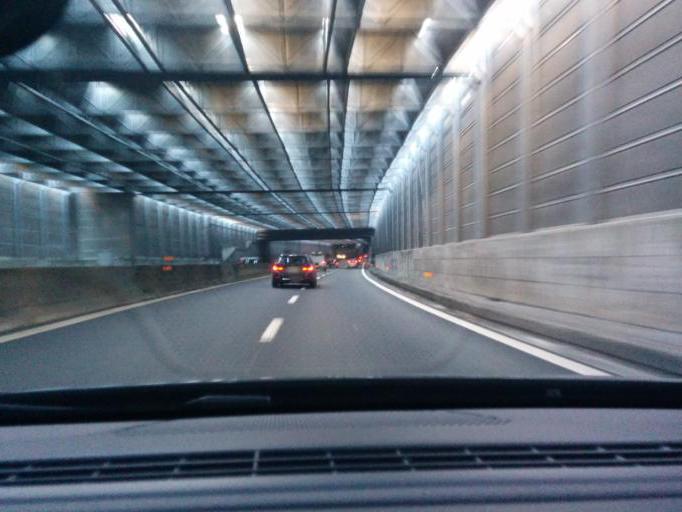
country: IT
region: Liguria
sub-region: Provincia di Genova
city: San Teodoro
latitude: 44.4303
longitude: 8.8466
